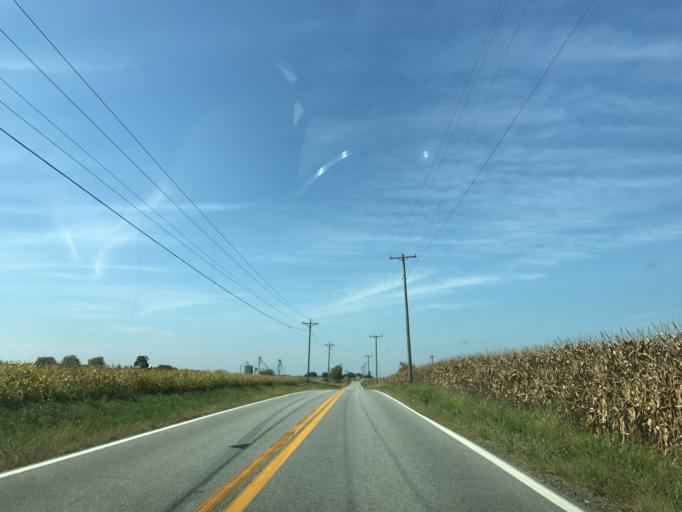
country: US
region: Maryland
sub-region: Queen Anne's County
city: Kingstown
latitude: 39.2744
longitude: -75.9446
